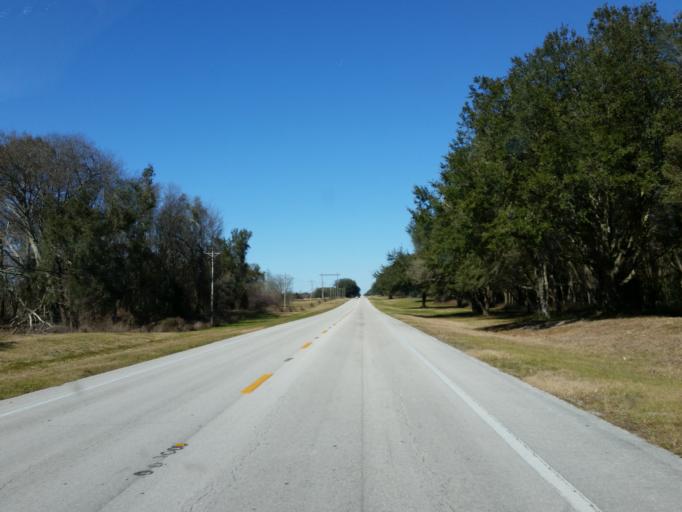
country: US
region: Florida
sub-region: Alachua County
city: Newberry
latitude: 29.6886
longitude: -82.6070
